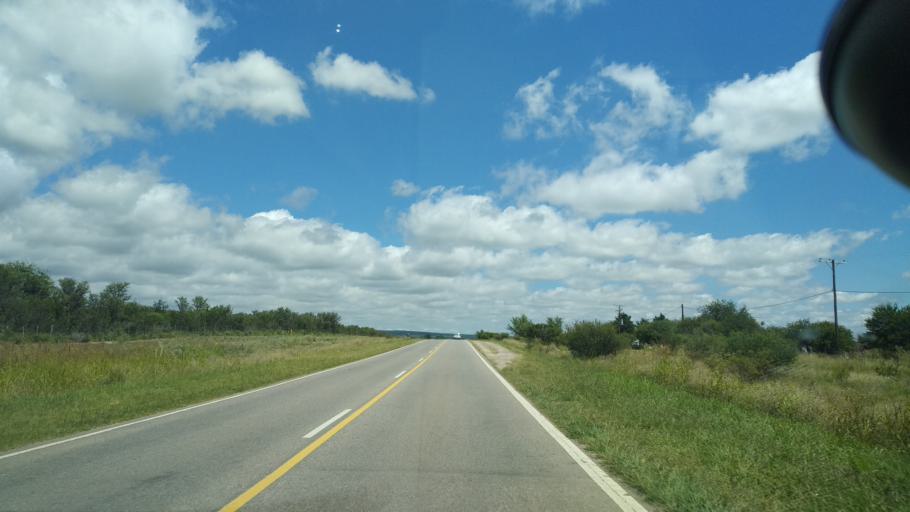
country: AR
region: Cordoba
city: Villa Cura Brochero
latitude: -31.6787
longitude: -65.0853
